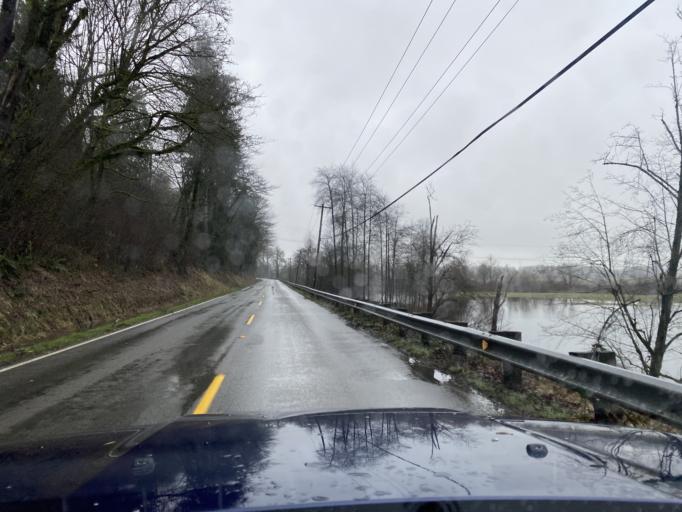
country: US
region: Washington
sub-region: King County
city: Duvall
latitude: 47.7985
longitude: -122.0013
